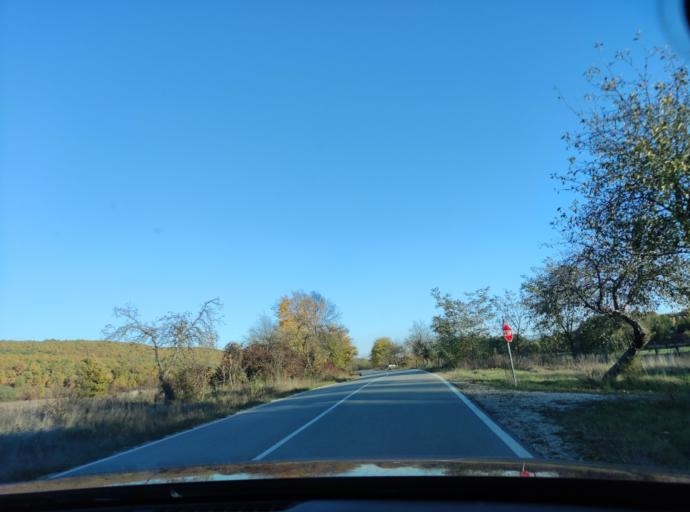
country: BG
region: Montana
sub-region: Obshtina Chiprovtsi
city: Chiprovtsi
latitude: 43.4179
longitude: 23.0267
